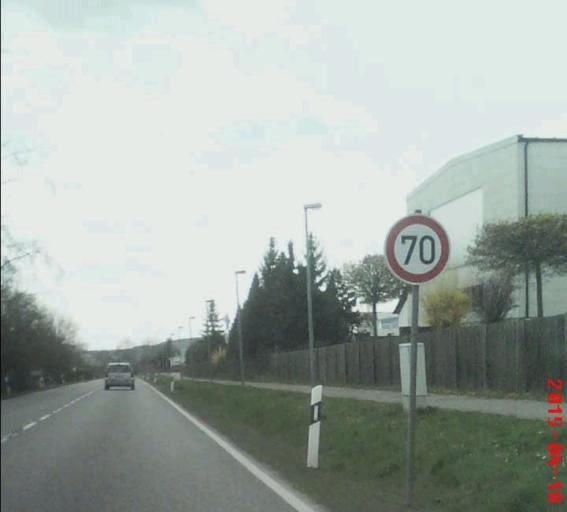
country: DE
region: Thuringia
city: Leinefelde
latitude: 51.3879
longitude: 10.3404
